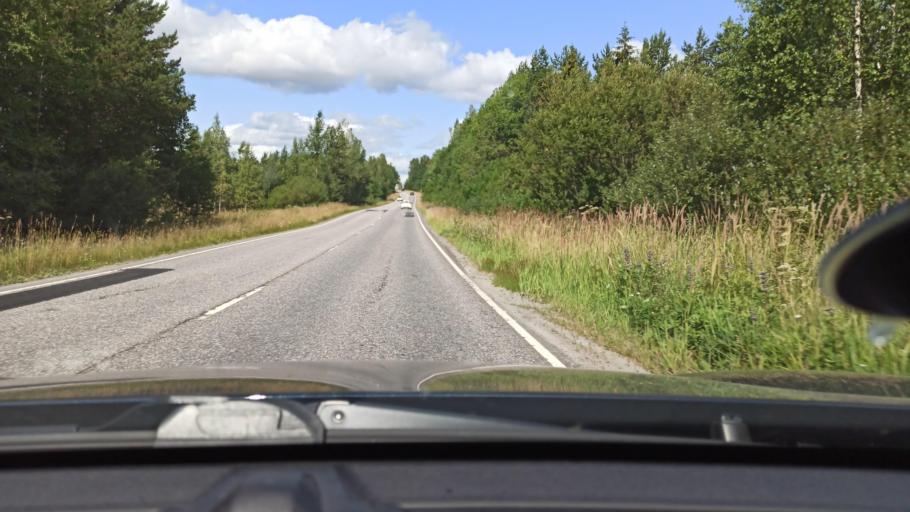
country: FI
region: Uusimaa
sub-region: Helsinki
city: Espoo
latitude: 60.1957
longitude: 24.5608
